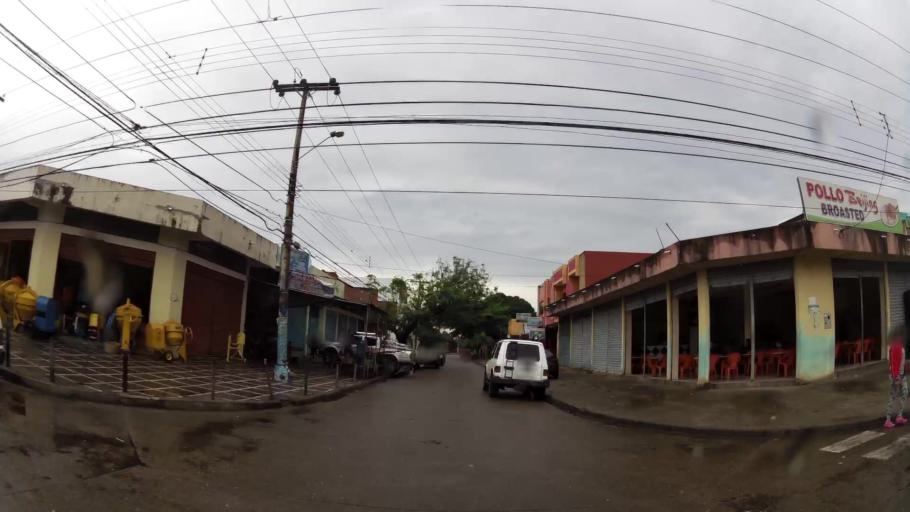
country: BO
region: Santa Cruz
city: Santa Cruz de la Sierra
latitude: -17.8106
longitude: -63.1873
